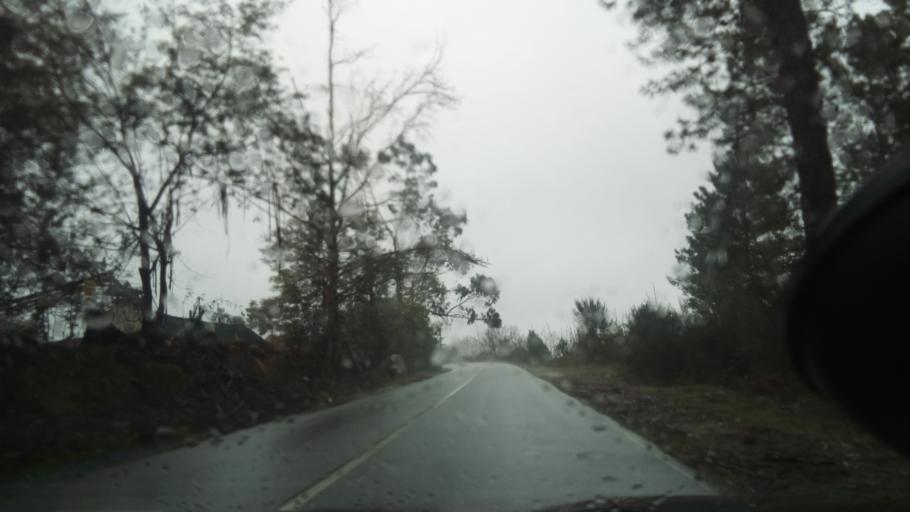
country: PT
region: Viseu
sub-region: Mangualde
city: Mangualde
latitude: 40.6103
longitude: -7.6941
